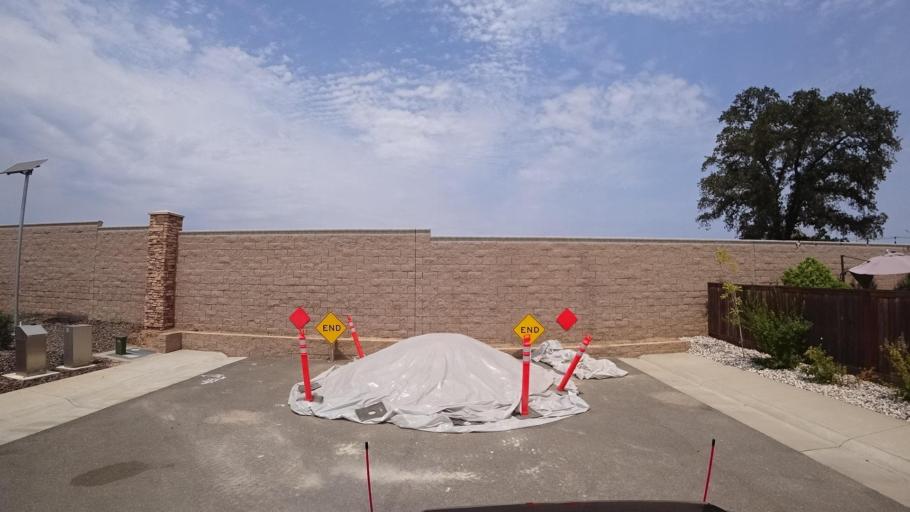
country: US
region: California
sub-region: Placer County
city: Loomis
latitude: 38.8066
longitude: -121.1996
